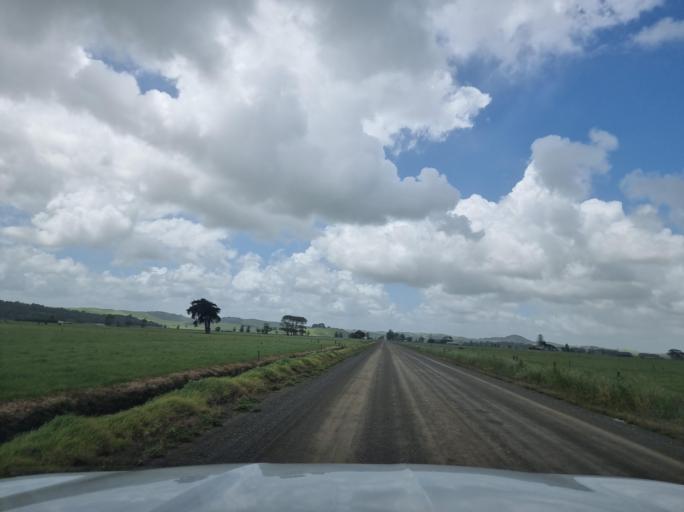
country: NZ
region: Northland
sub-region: Kaipara District
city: Dargaville
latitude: -36.0866
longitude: 174.0281
